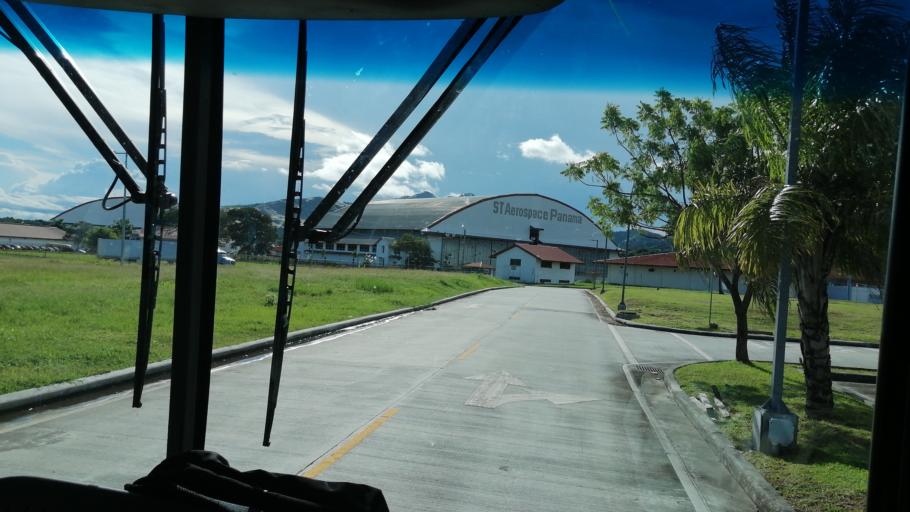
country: PA
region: Panama
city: Veracruz
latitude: 8.9170
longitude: -79.5935
